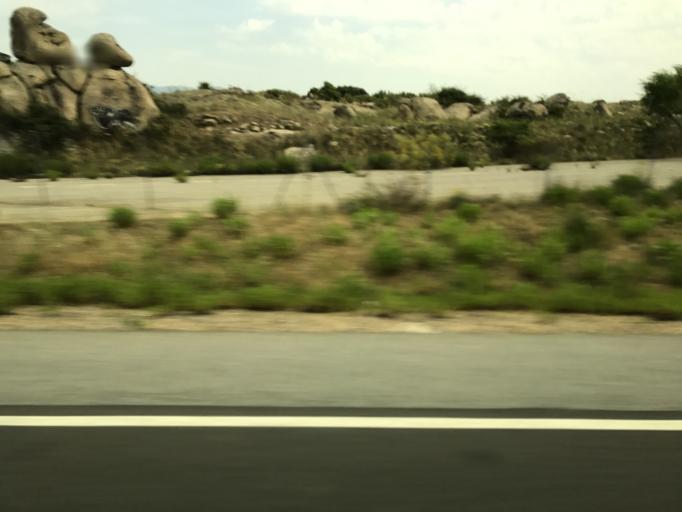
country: ES
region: Madrid
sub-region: Provincia de Madrid
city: La Cabrera
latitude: 40.9014
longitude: -3.6077
